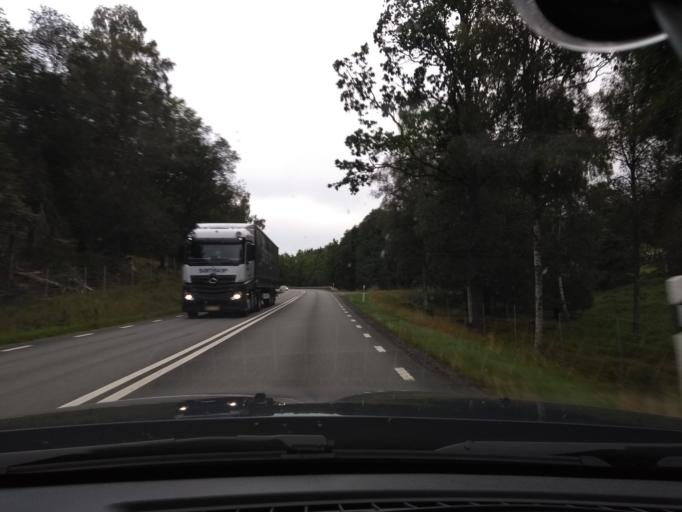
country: SE
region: Joenkoeping
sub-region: Eksjo Kommun
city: Eksjoe
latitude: 57.6383
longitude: 14.8459
